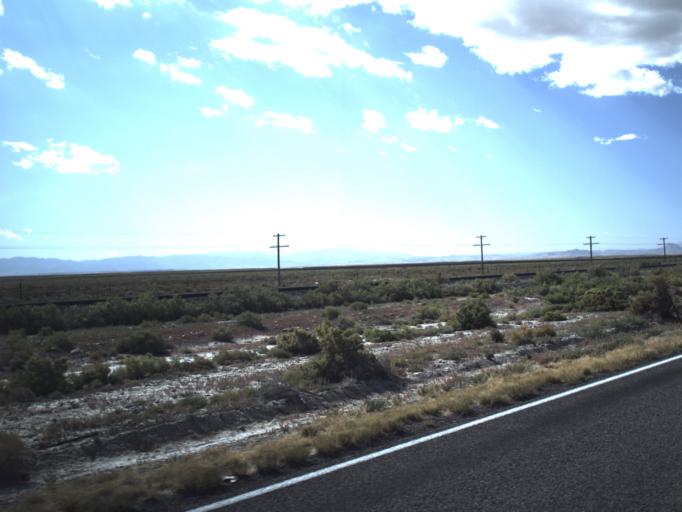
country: US
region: Utah
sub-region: Millard County
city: Delta
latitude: 39.0434
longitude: -112.7703
